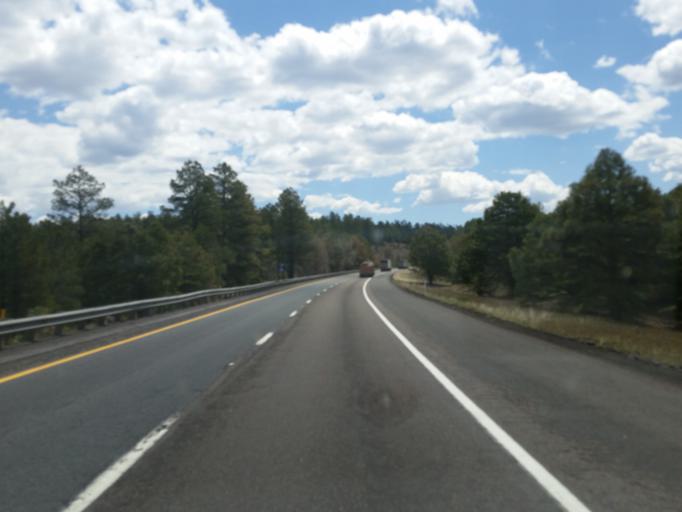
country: US
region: Arizona
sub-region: Coconino County
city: Parks
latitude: 35.2523
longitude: -111.9045
